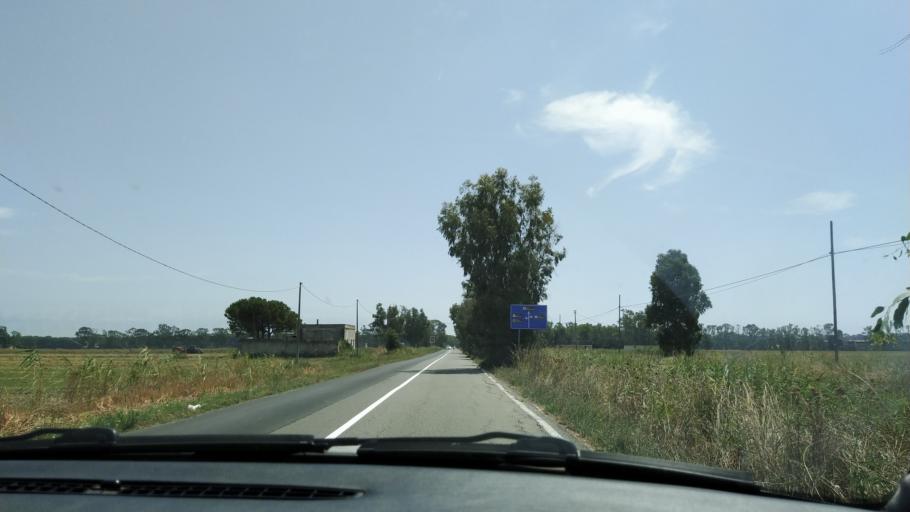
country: IT
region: Basilicate
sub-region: Provincia di Matera
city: Marconia
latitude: 40.3288
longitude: 16.7852
